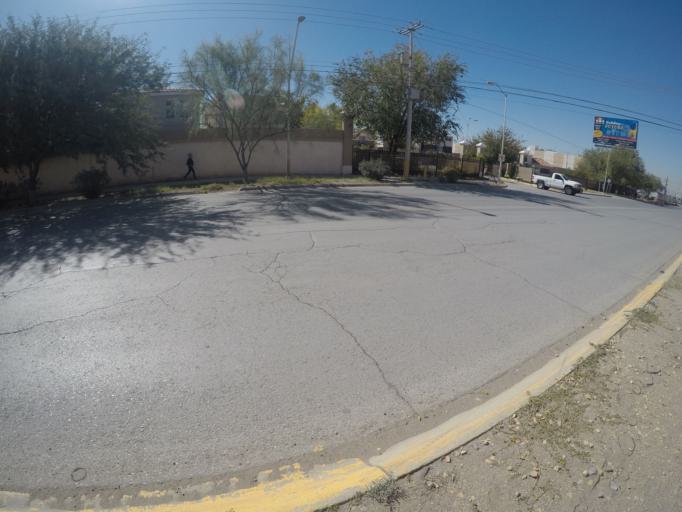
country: US
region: Texas
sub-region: El Paso County
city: Socorro
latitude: 31.6946
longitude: -106.3766
